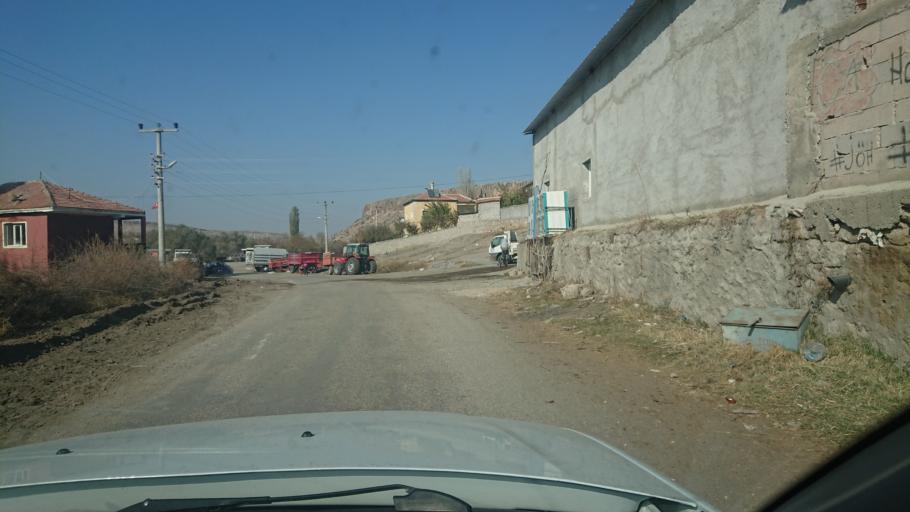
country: TR
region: Aksaray
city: Gulagac
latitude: 38.3541
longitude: 34.2321
